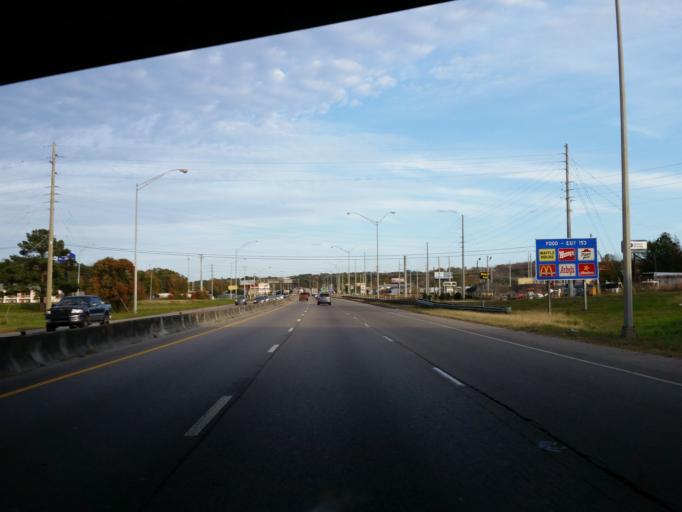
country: US
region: Mississippi
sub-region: Lauderdale County
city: Meridian
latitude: 32.3490
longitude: -88.7105
